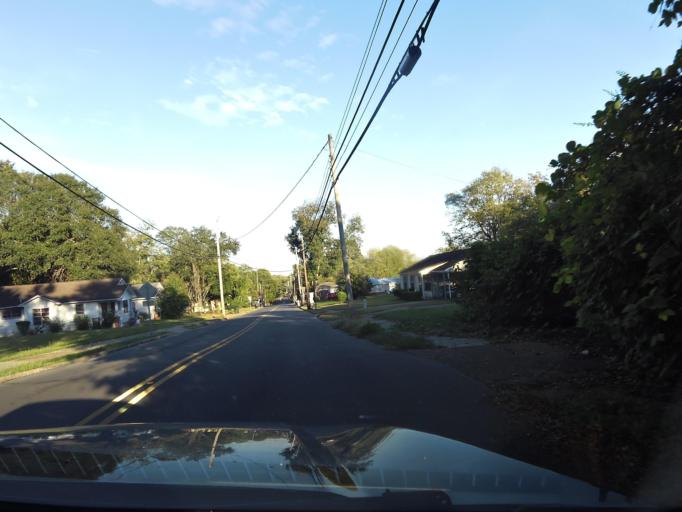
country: US
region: Alabama
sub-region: Houston County
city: Dothan
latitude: 31.2277
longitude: -85.3851
